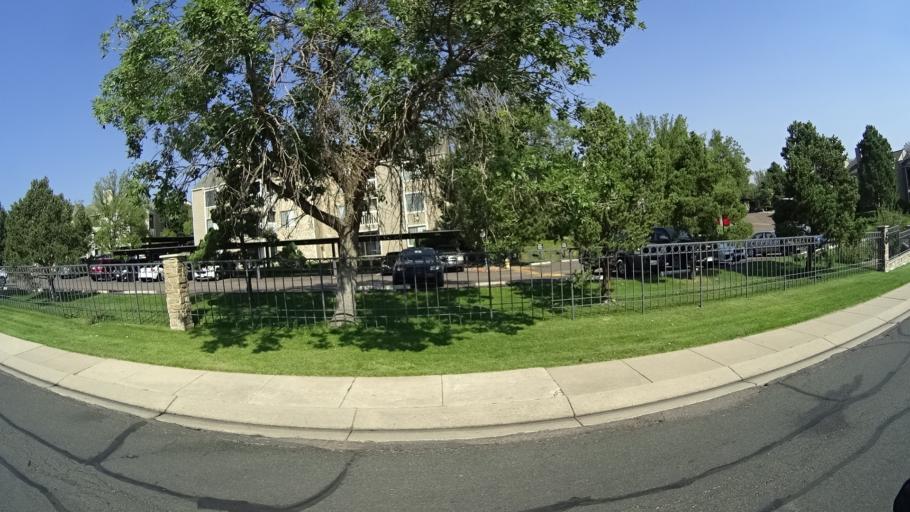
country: US
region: Colorado
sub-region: El Paso County
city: Stratmoor
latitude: 38.7832
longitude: -104.8072
